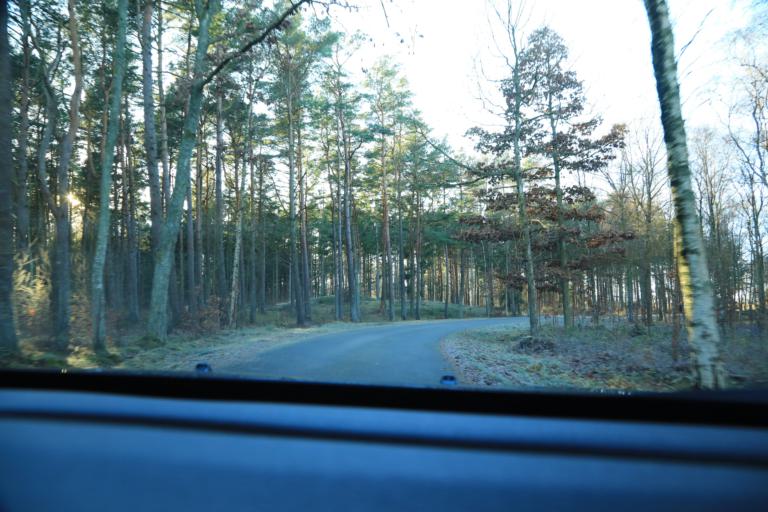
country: SE
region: Halland
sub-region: Kungsbacka Kommun
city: Frillesas
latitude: 57.1972
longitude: 12.1709
